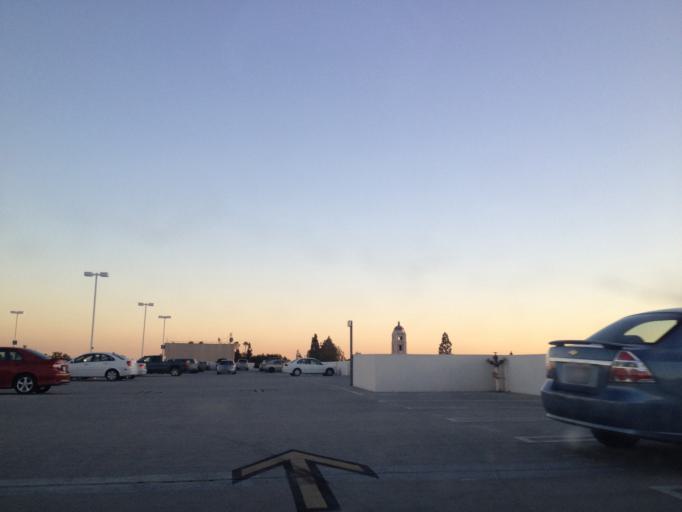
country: US
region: California
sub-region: Orange County
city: Fullerton
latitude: 33.8773
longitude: -117.9196
